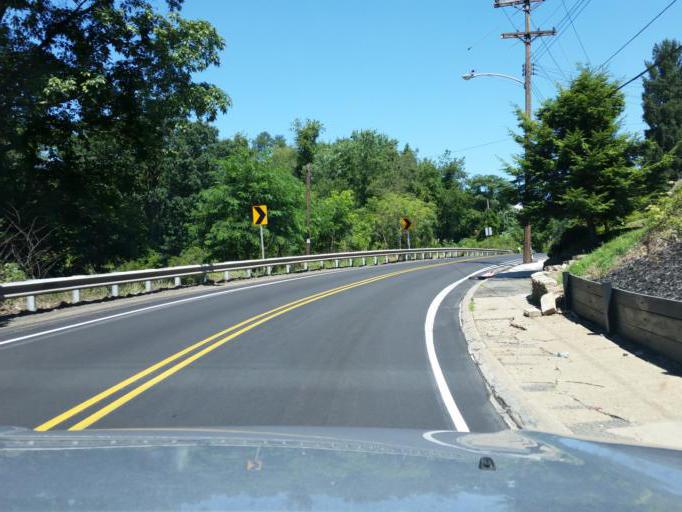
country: US
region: Pennsylvania
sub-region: Allegheny County
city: Churchill
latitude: 40.4529
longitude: -79.8447
